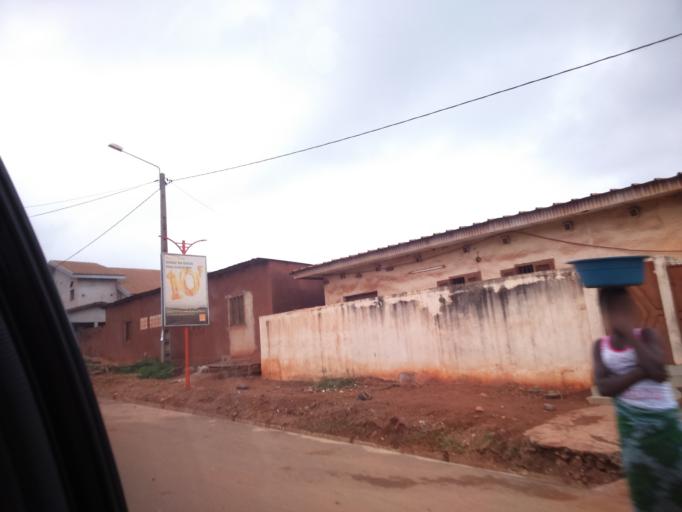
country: CI
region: Moyen-Comoe
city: Abengourou
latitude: 6.7245
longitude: -3.4869
